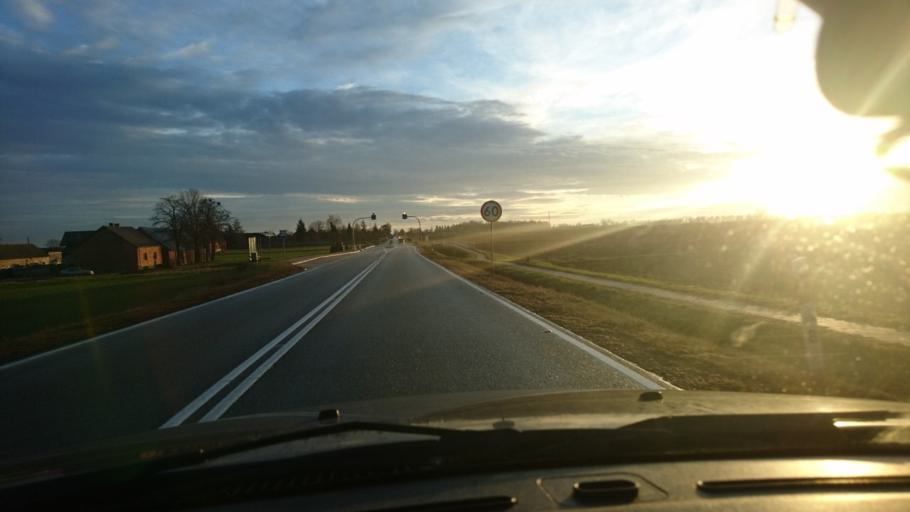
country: PL
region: Greater Poland Voivodeship
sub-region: Powiat kepinski
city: Opatow
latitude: 51.1928
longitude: 18.1481
